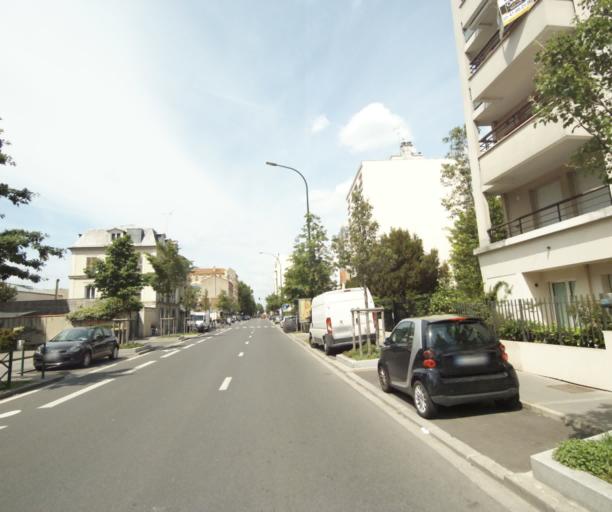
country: FR
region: Ile-de-France
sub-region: Departement des Hauts-de-Seine
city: Colombes
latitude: 48.9168
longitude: 2.2527
